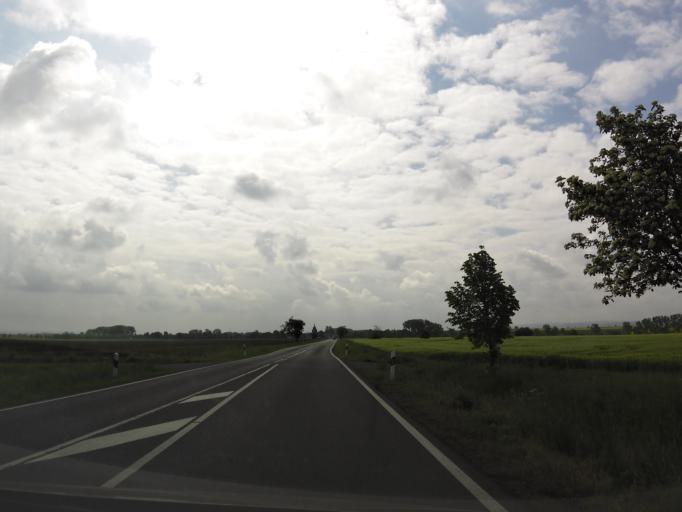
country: DE
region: Thuringia
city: Grabsleben
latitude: 50.9296
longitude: 10.8501
